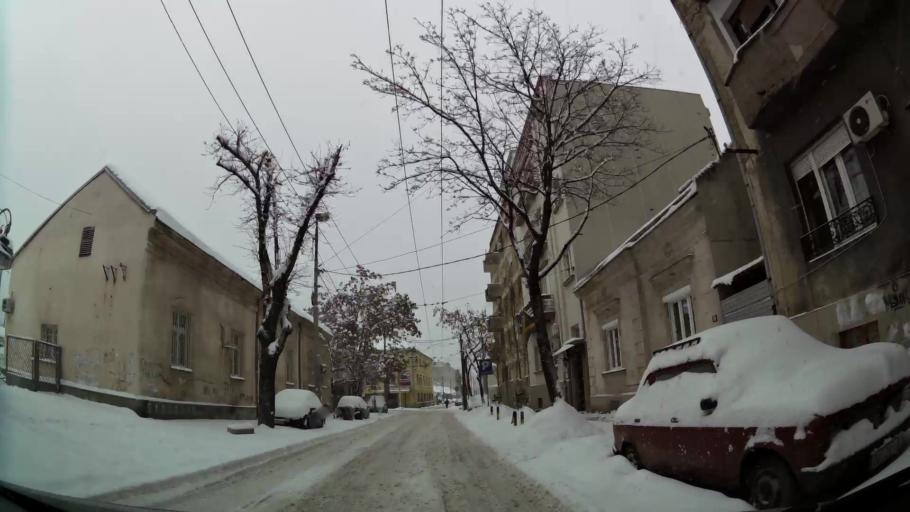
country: RS
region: Central Serbia
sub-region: Belgrade
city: Stari Grad
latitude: 44.8220
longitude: 20.4659
